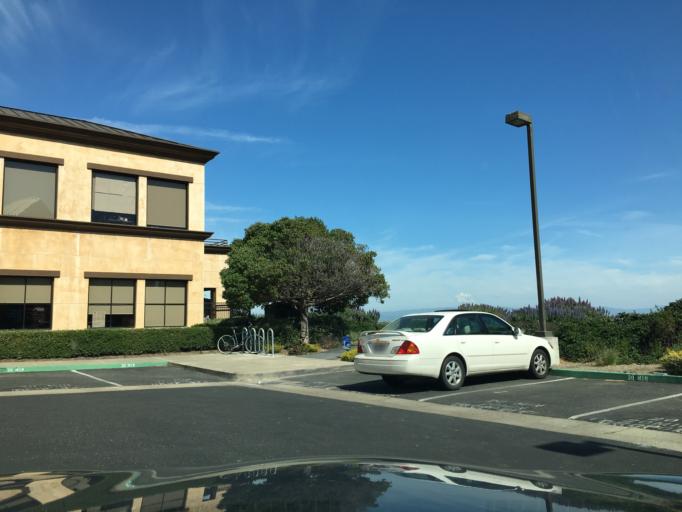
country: US
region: California
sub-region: San Mateo County
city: Redwood Shores
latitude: 37.5185
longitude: -122.2489
